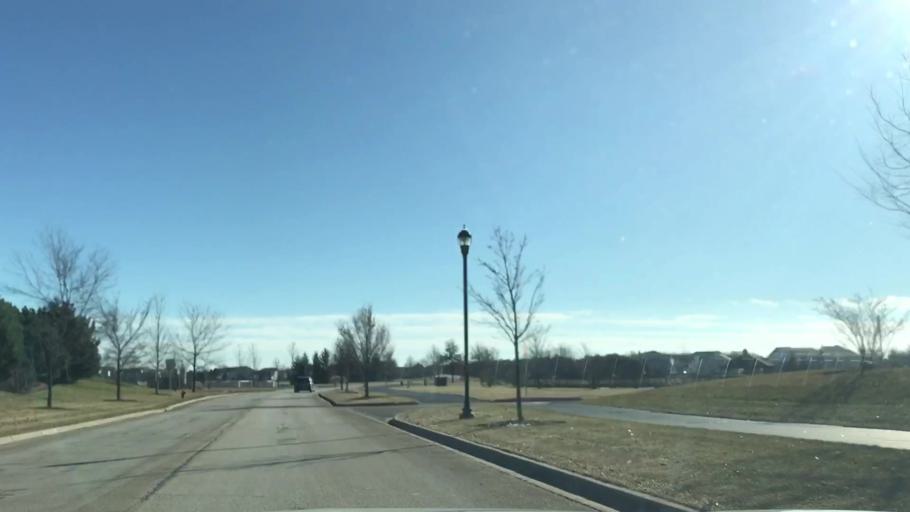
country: US
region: Illinois
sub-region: Kane County
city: Pingree Grove
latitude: 42.0841
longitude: -88.4325
